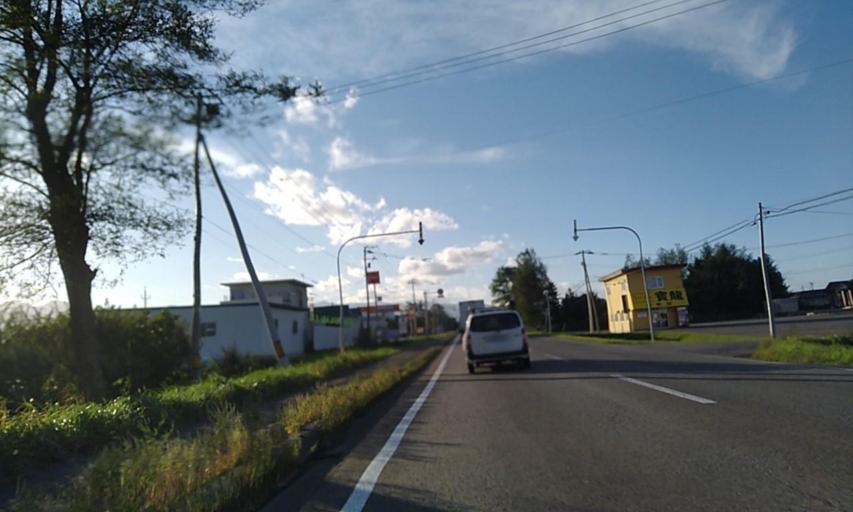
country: JP
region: Hokkaido
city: Otofuke
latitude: 42.9437
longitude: 142.9480
